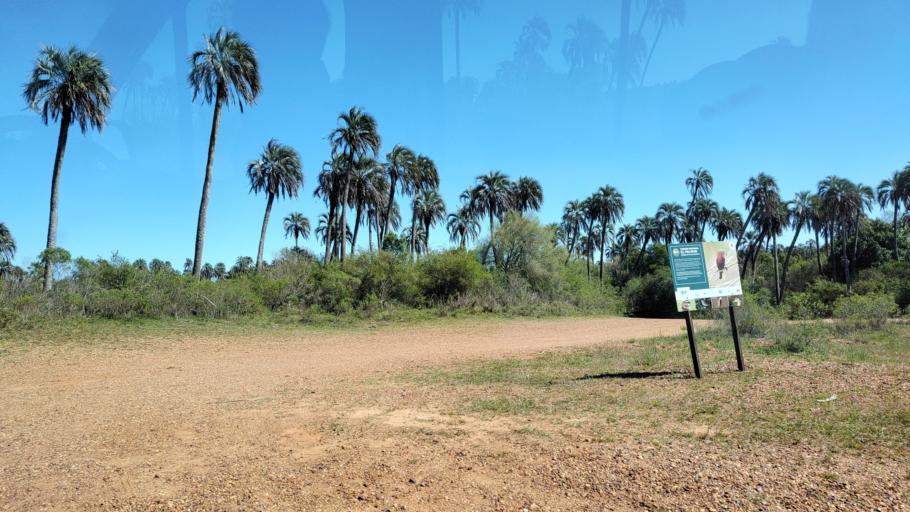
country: AR
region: Entre Rios
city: Ubajay
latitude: -31.8861
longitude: -58.2399
